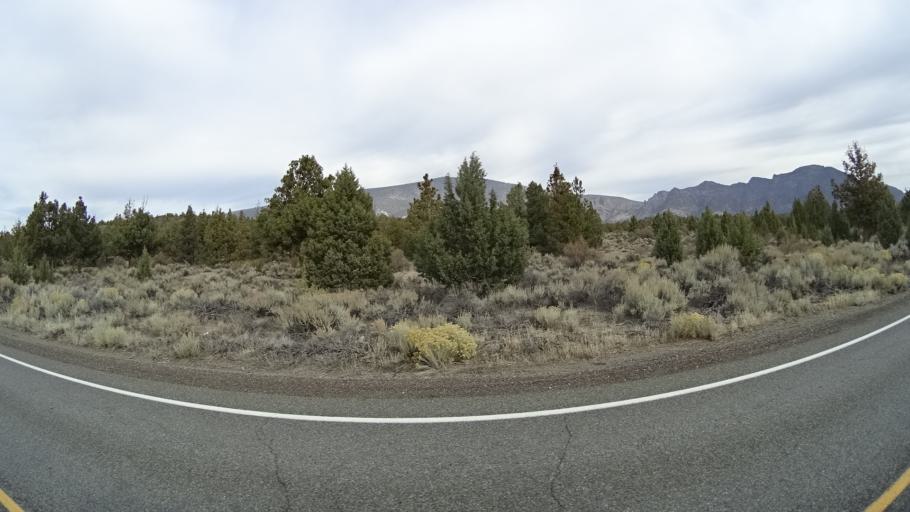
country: US
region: California
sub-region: Siskiyou County
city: Weed
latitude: 41.5742
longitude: -122.2791
